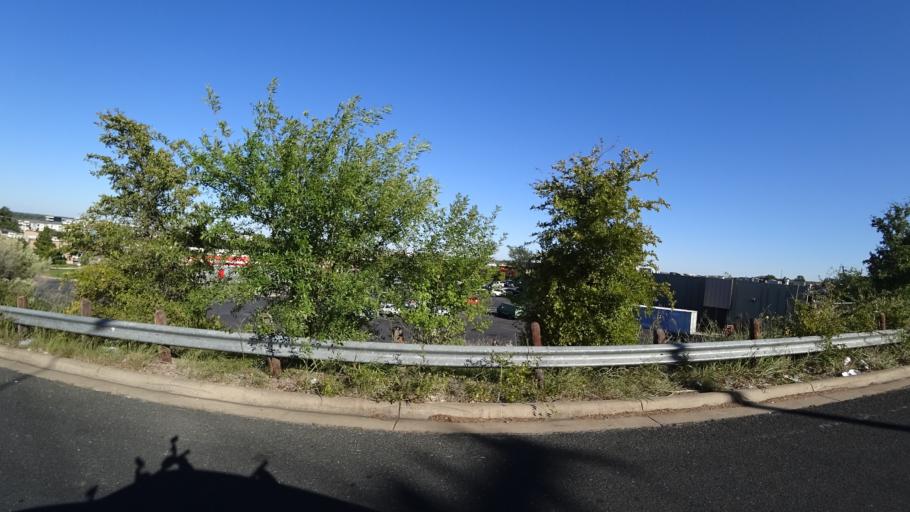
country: US
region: Texas
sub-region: Travis County
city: Austin
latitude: 30.2386
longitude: -97.7279
